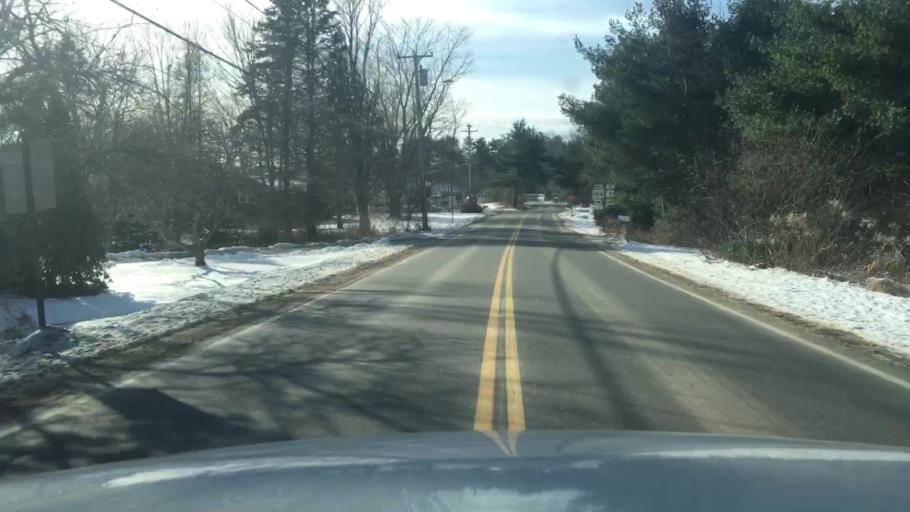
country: US
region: Maine
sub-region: Lincoln County
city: Wiscasset
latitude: 43.9633
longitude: -69.6995
